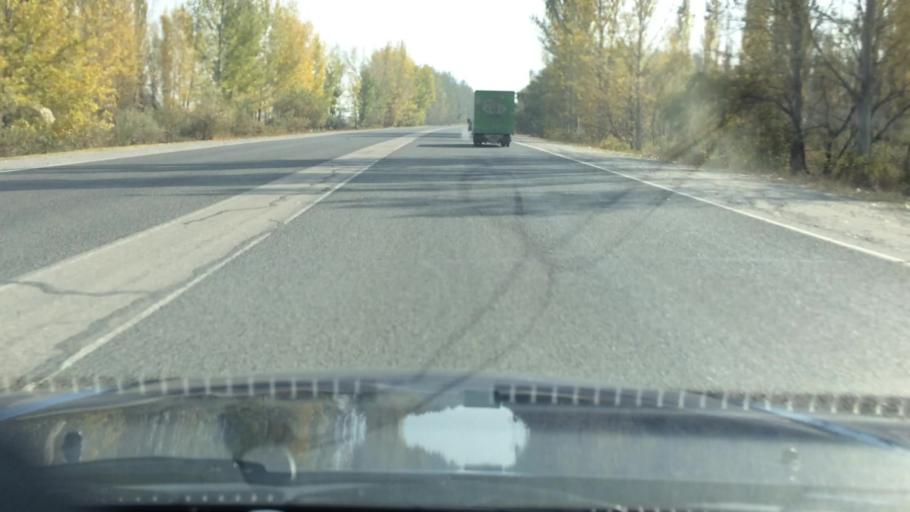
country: KG
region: Chuy
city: Ivanovka
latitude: 42.9370
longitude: 74.9882
